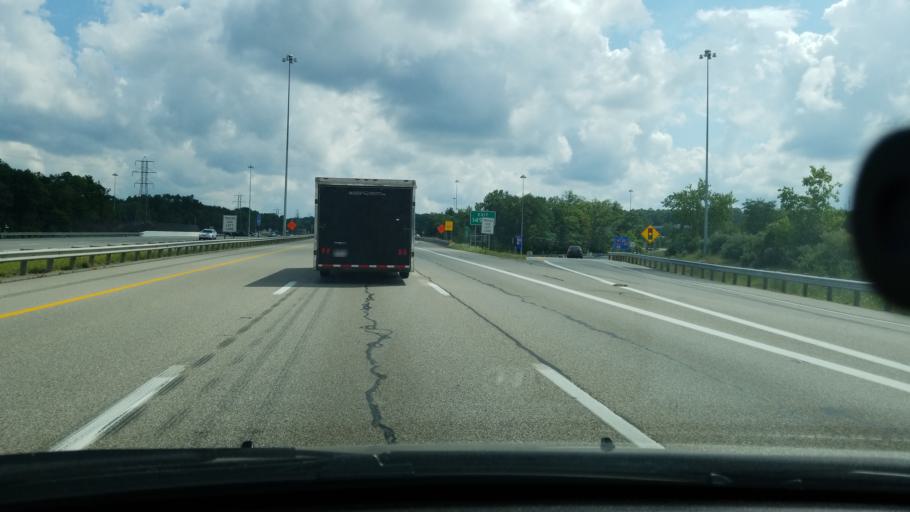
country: US
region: Ohio
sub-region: Cuyahoga County
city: Brecksville
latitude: 41.3184
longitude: -81.6491
